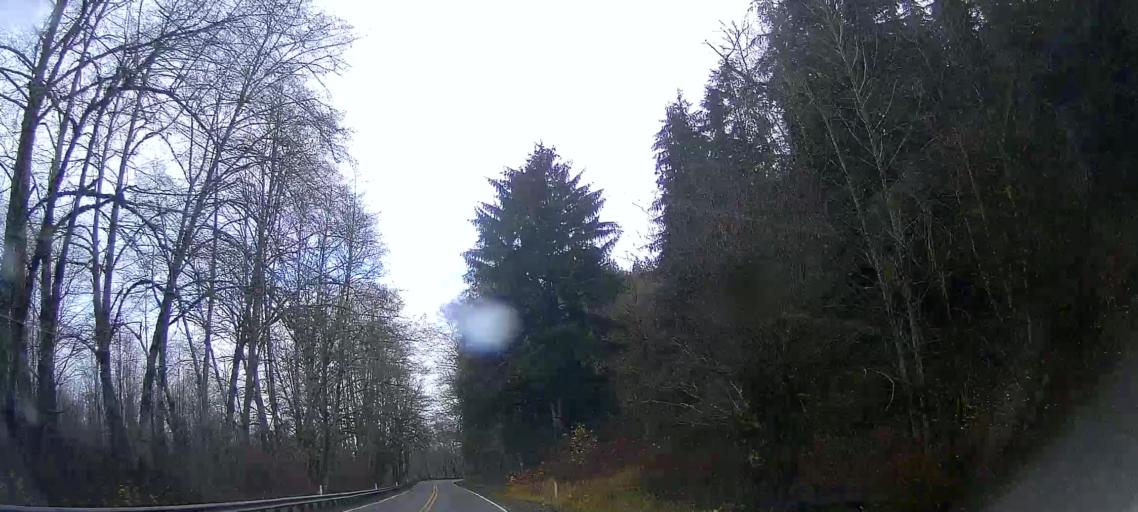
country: US
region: Washington
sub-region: Skagit County
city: Sedro-Woolley
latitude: 48.5139
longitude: -121.9883
